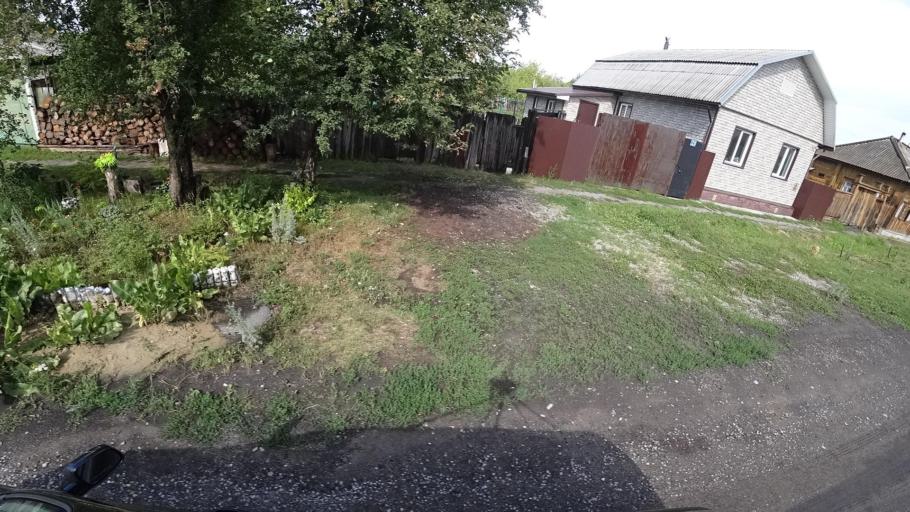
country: RU
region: Sverdlovsk
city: Kamyshlov
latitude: 56.8414
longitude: 62.7288
